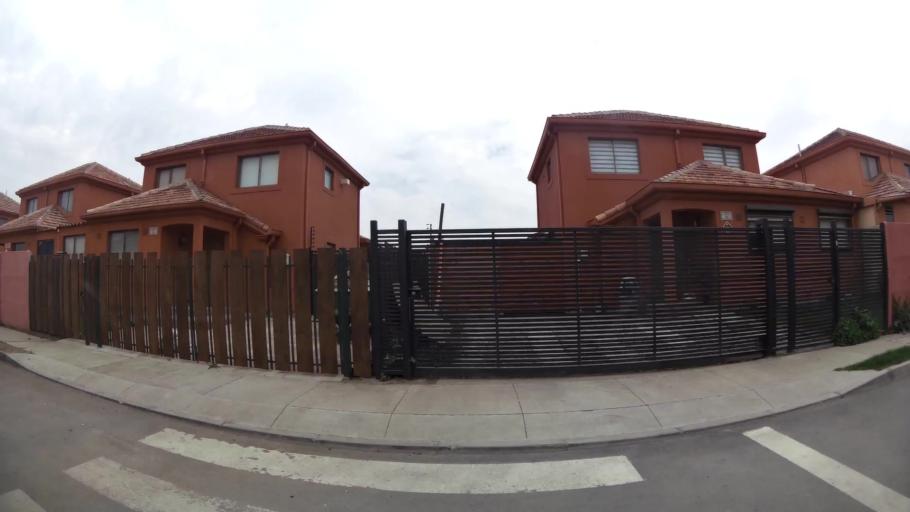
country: CL
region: Santiago Metropolitan
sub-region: Provincia de Chacabuco
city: Chicureo Abajo
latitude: -33.2162
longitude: -70.6686
